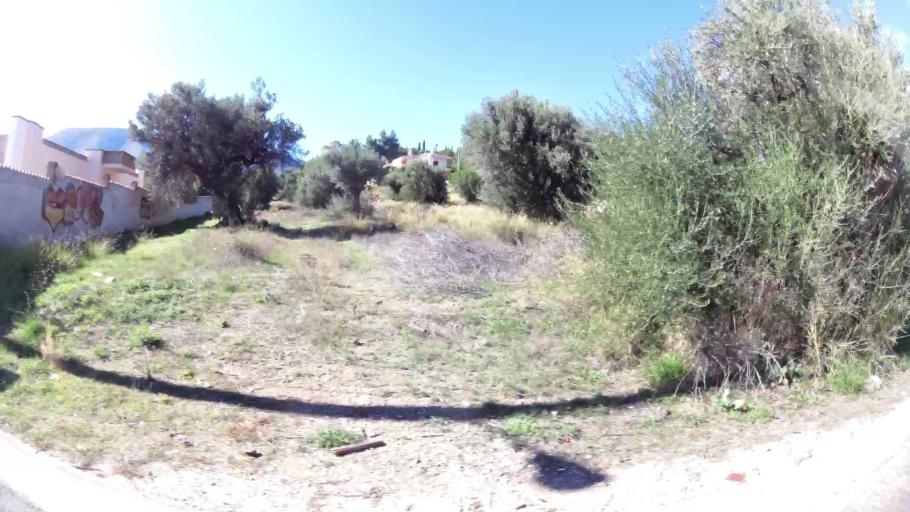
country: GR
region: Attica
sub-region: Nomarchia Anatolikis Attikis
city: Paiania
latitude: 37.9589
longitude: 23.8630
